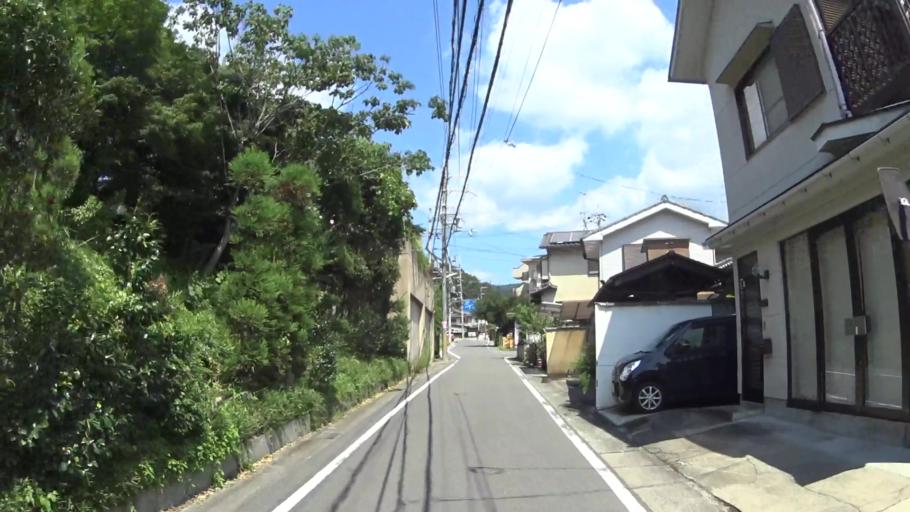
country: JP
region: Kyoto
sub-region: Kyoto-shi
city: Kamigyo-ku
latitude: 35.0758
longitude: 135.7653
